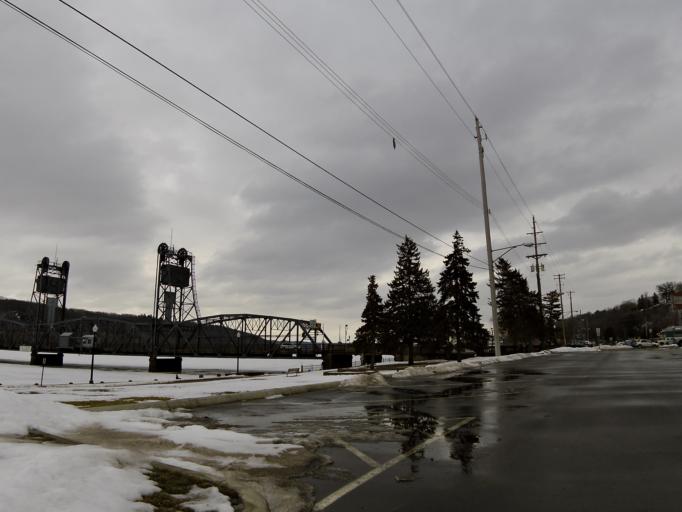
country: US
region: Minnesota
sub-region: Washington County
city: Stillwater
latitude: 45.0568
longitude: -92.8048
